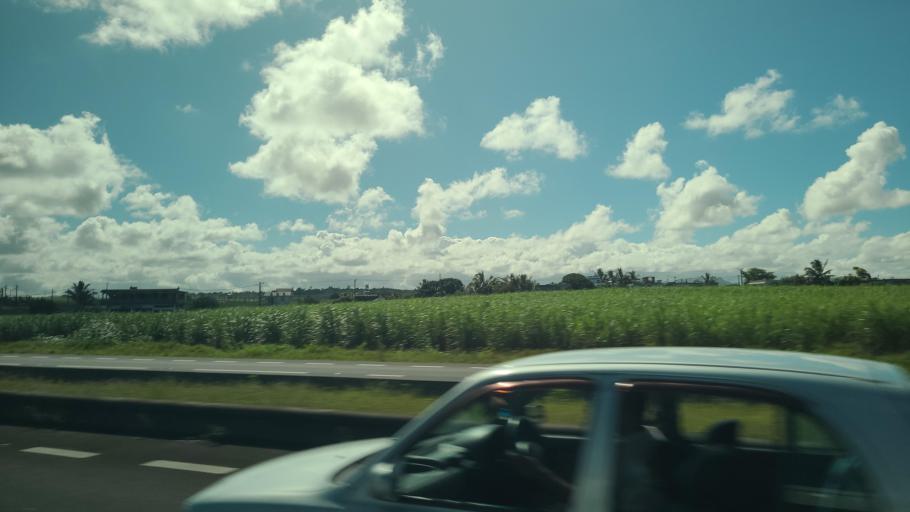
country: MU
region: Grand Port
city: Plaine Magnien
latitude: -20.4395
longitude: 57.6578
